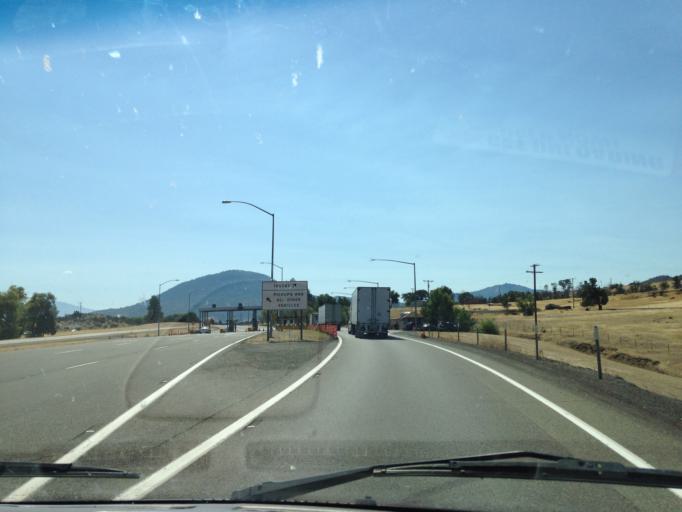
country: US
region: California
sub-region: Siskiyou County
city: Yreka
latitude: 41.9274
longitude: -122.5811
